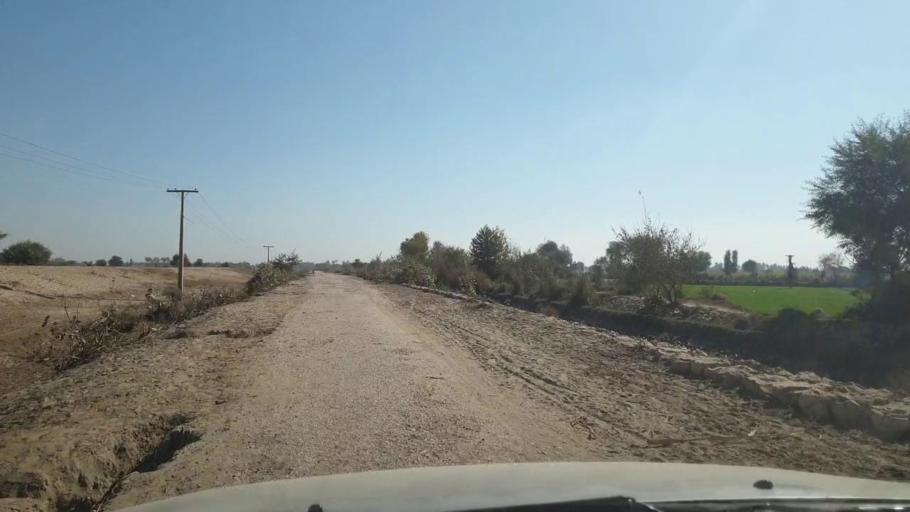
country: PK
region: Sindh
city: Ghotki
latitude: 28.0846
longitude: 69.3405
